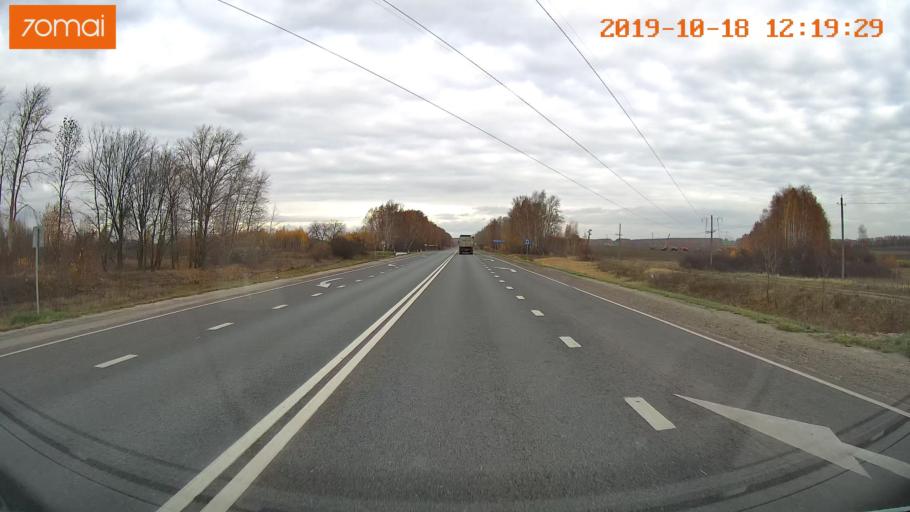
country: RU
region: Rjazan
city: Zakharovo
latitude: 54.4830
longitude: 39.4686
